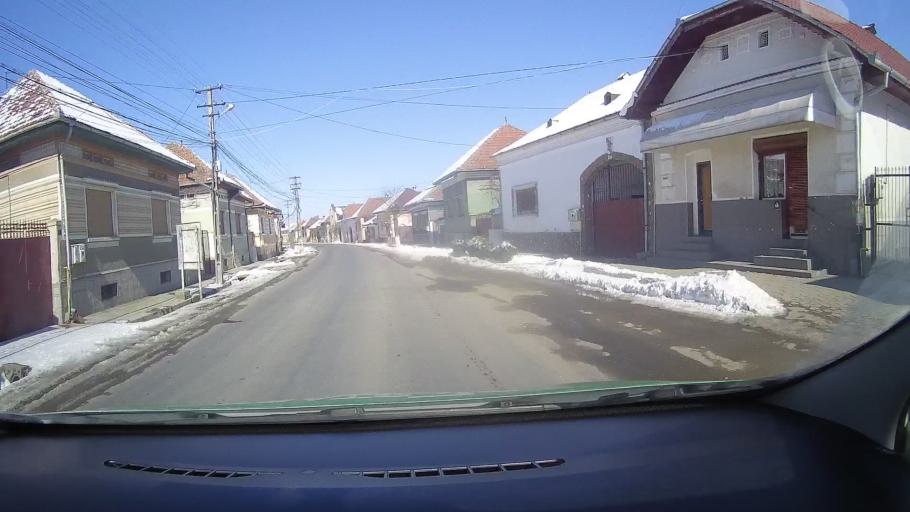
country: RO
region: Brasov
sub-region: Comuna Harseni
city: Harseni
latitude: 45.7896
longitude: 24.9975
